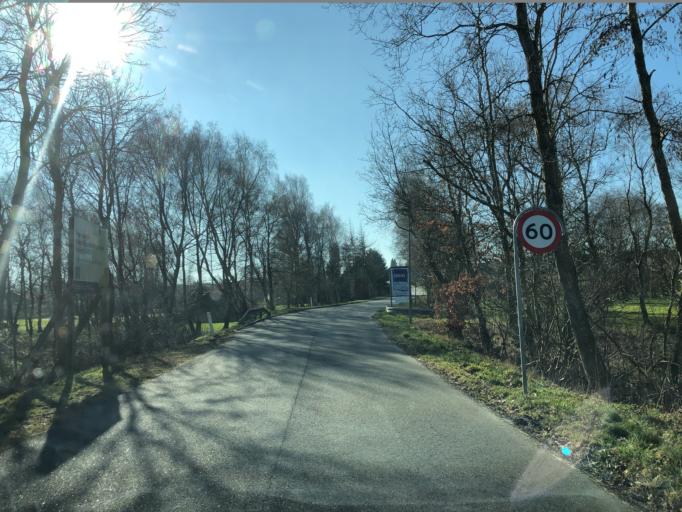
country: DK
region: Central Jutland
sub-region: Ikast-Brande Kommune
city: Bording Kirkeby
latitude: 56.1507
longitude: 9.2803
